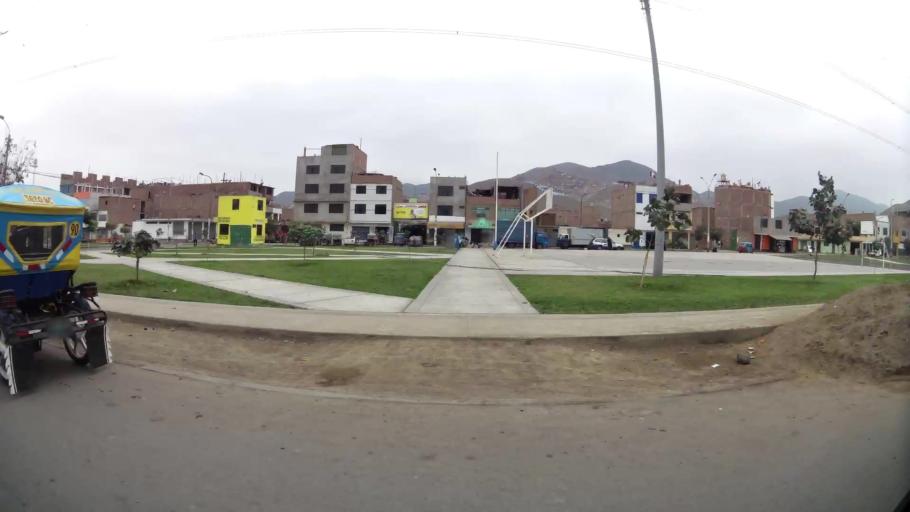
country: PE
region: Lima
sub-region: Lima
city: Independencia
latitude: -11.9350
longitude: -77.0835
